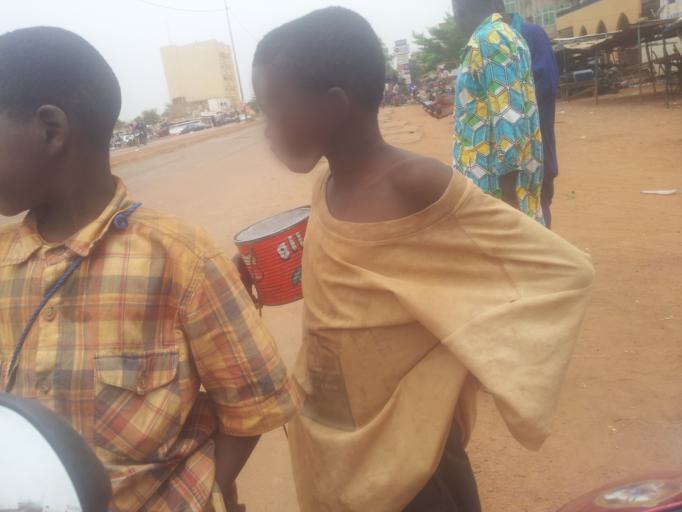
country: BF
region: Centre
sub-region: Kadiogo Province
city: Ouagadougou
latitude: 12.3878
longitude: -1.5655
